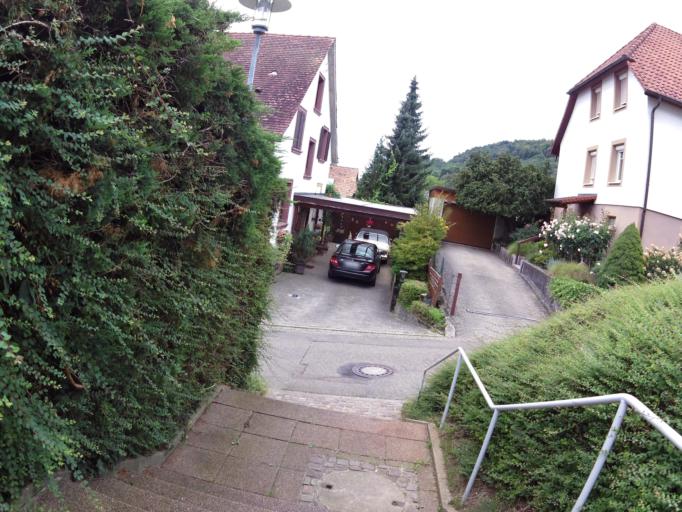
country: DE
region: Baden-Wuerttemberg
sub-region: Freiburg Region
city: Hohberg
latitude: 48.3392
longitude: 7.9074
